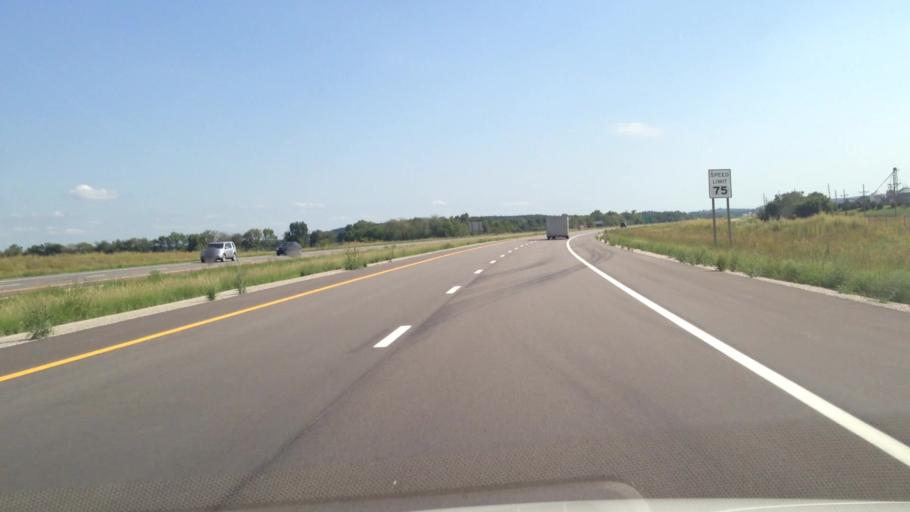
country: US
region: Kansas
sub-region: Linn County
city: La Cygne
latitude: 38.3355
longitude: -94.6783
